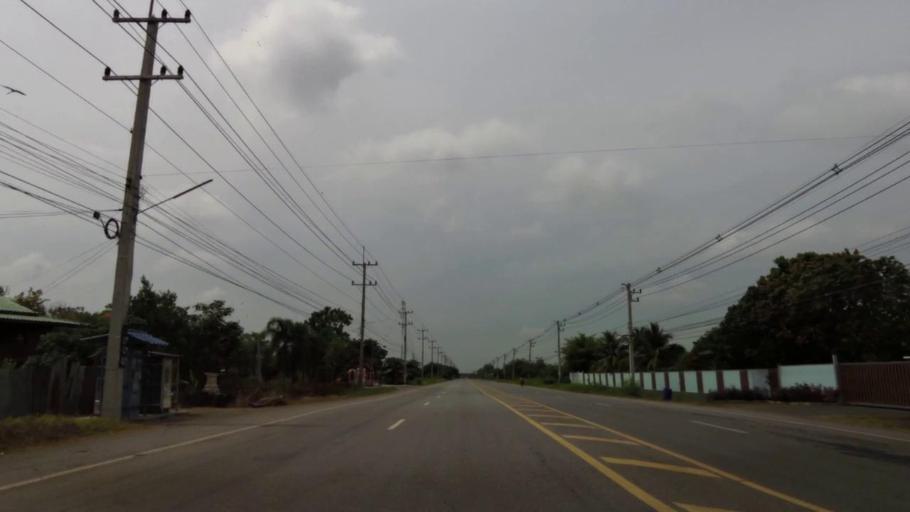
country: TH
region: Lop Buri
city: Ban Mi
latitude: 15.0612
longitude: 100.6045
